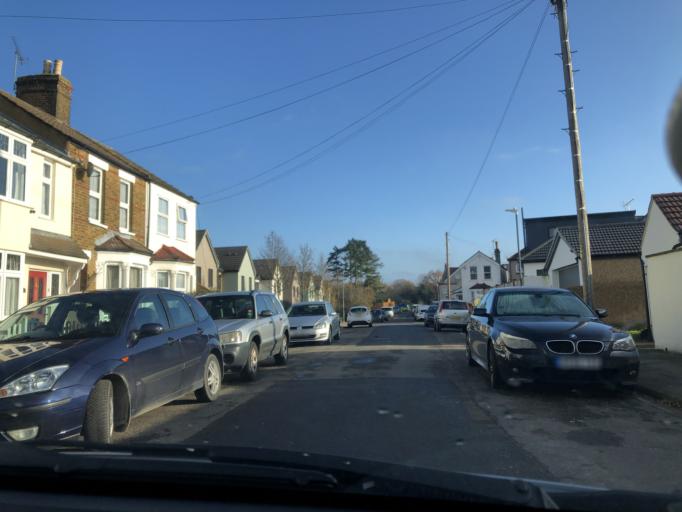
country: GB
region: England
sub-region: Greater London
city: Bexley
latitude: 51.4366
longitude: 0.1709
